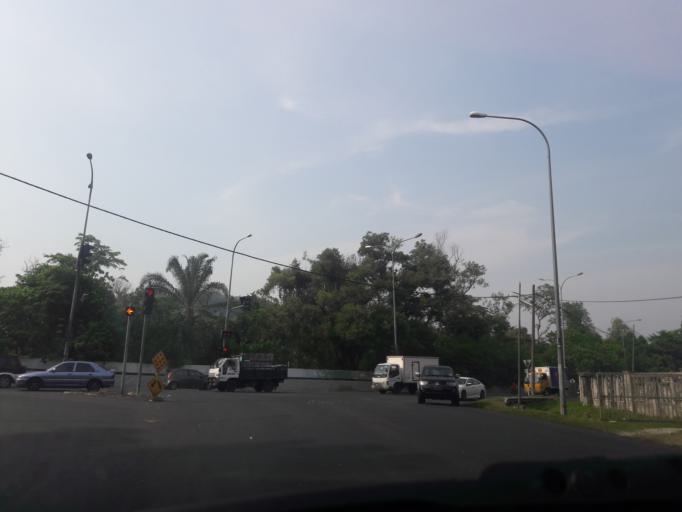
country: MY
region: Kedah
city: Kulim
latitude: 5.3462
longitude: 100.5197
